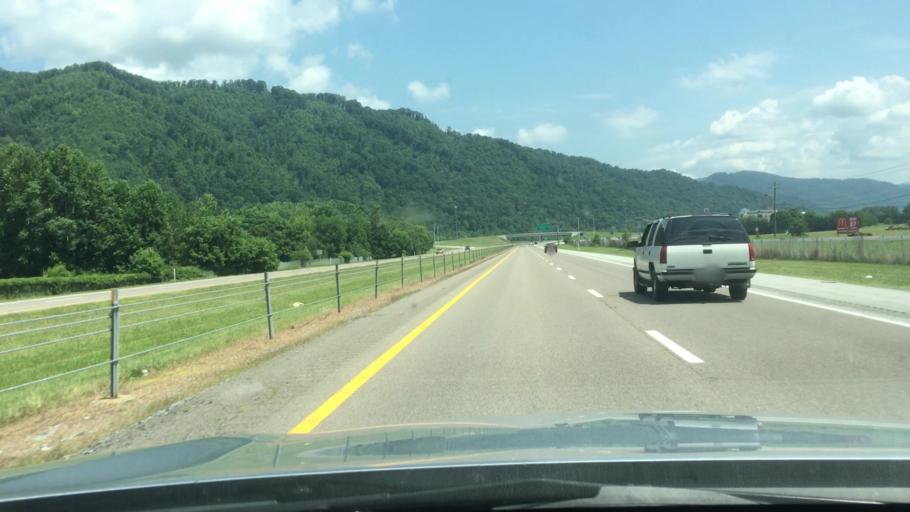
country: US
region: Tennessee
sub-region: Unicoi County
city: Banner Hill
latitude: 36.1155
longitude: -82.4486
